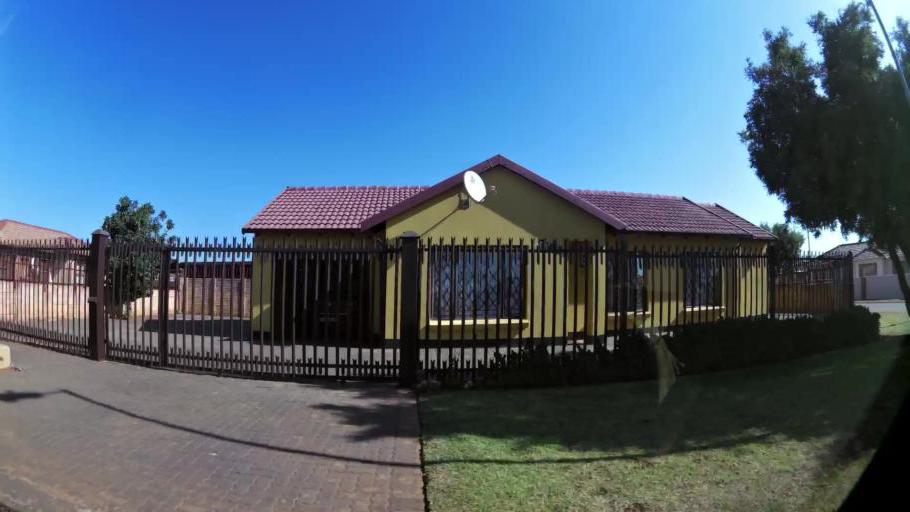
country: ZA
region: North-West
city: Ga-Rankuwa
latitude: -25.6371
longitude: 28.0840
